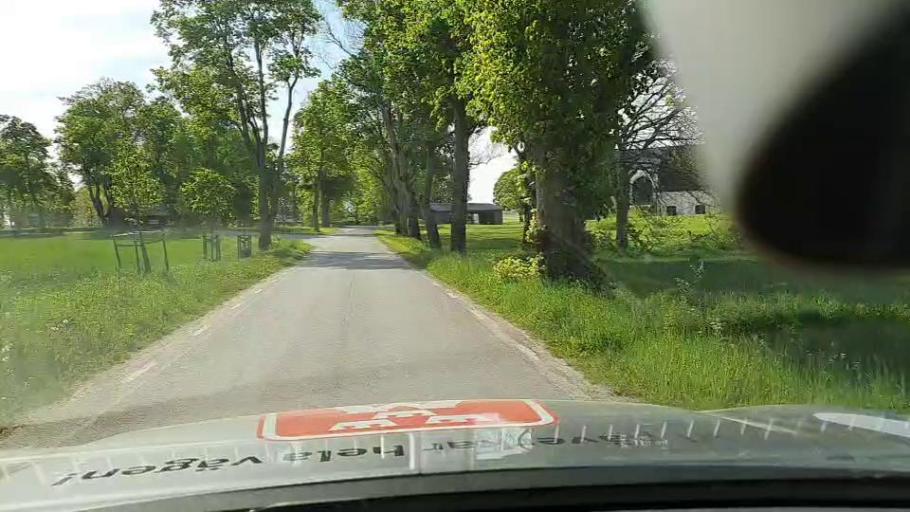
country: SE
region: Soedermanland
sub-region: Eskilstuna Kommun
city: Arla
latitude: 59.2587
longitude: 16.6541
